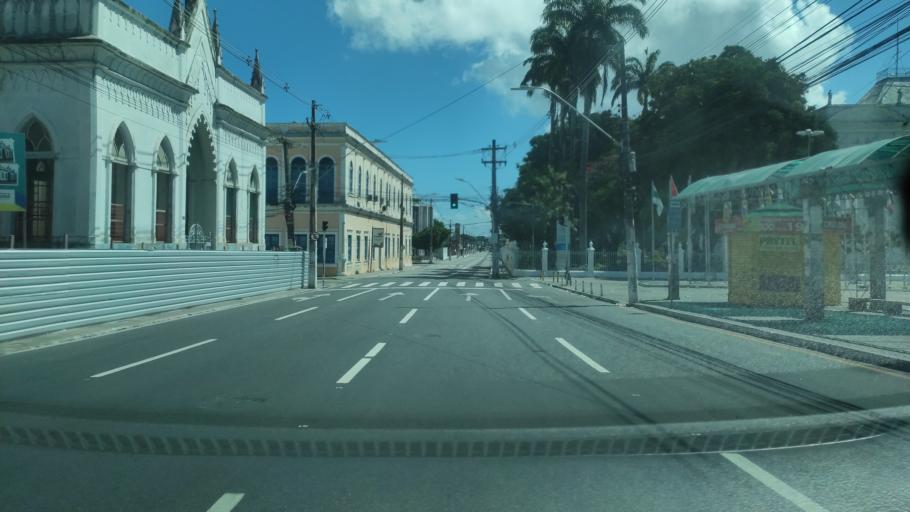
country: BR
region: Alagoas
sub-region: Maceio
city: Maceio
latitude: -9.6604
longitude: -35.7389
